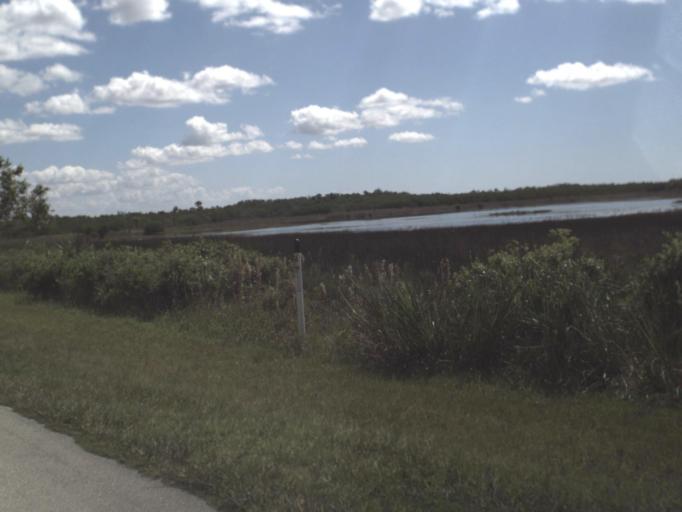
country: US
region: Florida
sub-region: Collier County
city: Lely Resort
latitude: 25.9864
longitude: -81.5692
